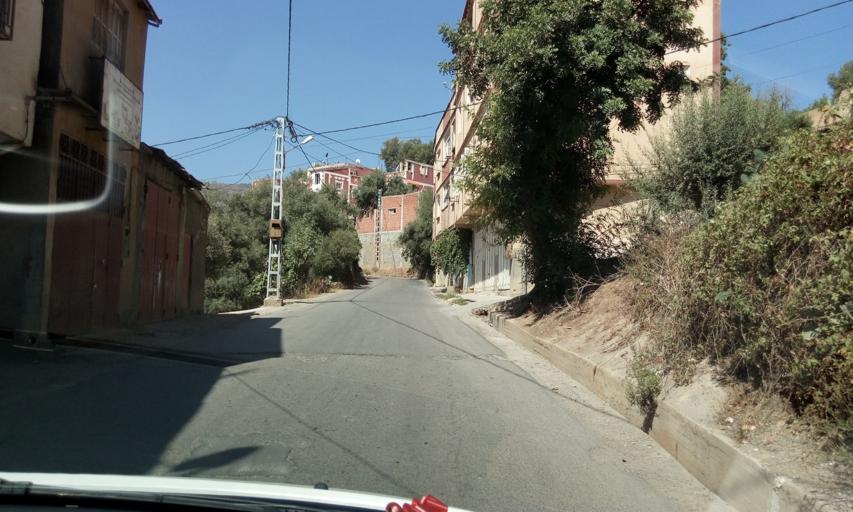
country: DZ
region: Tizi Ouzou
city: Chemini
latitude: 36.6061
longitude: 4.6493
